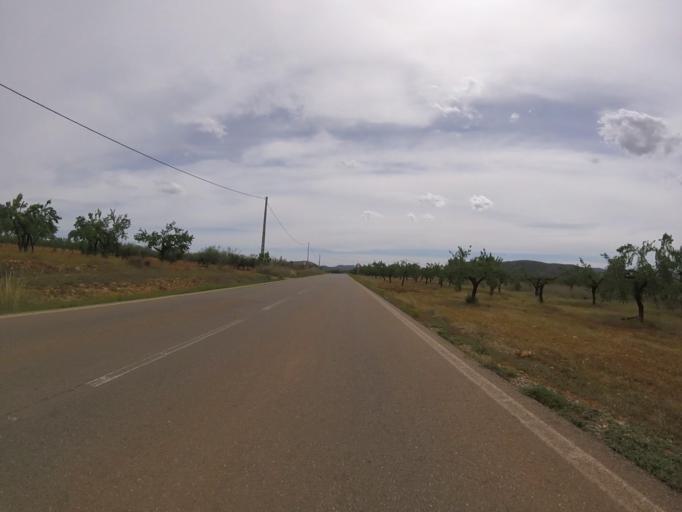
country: ES
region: Valencia
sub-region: Provincia de Castello
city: Cabanes
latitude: 40.1686
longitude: 0.0019
